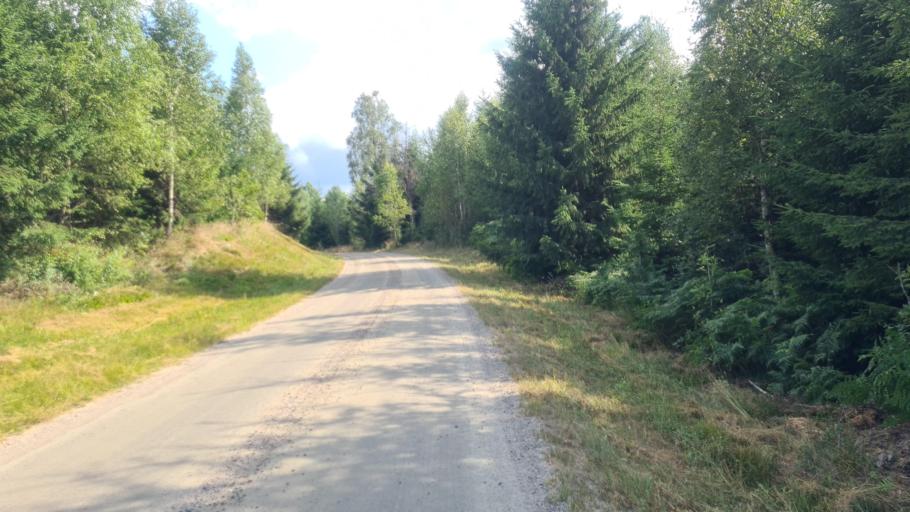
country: SE
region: Kronoberg
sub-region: Ljungby Kommun
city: Ljungby
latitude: 56.7257
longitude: 13.8844
